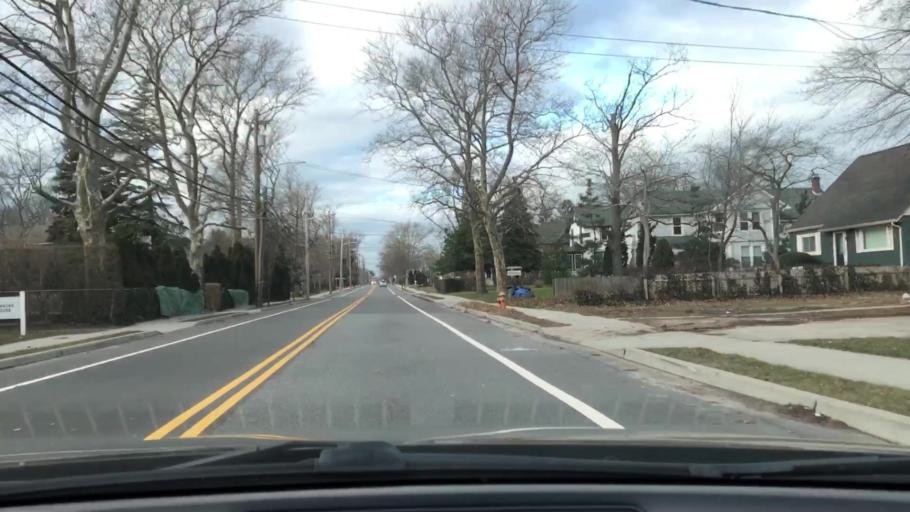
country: US
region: New York
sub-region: Suffolk County
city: Riverhead
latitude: 40.9285
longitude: -72.6703
